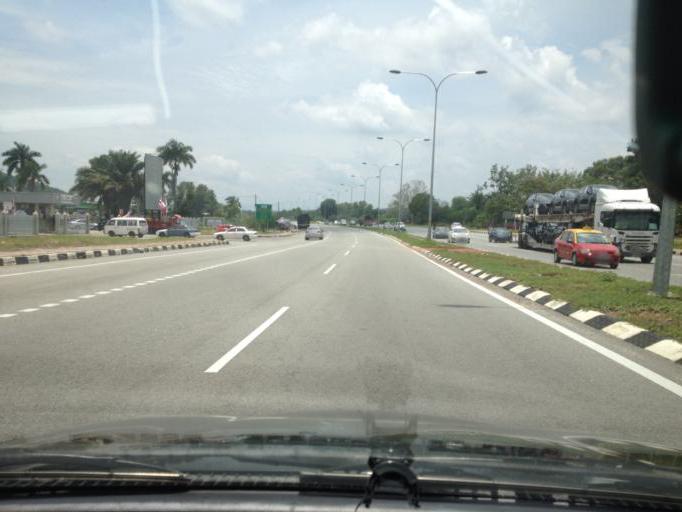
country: MY
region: Kedah
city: Sungai Petani
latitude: 5.6235
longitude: 100.5357
